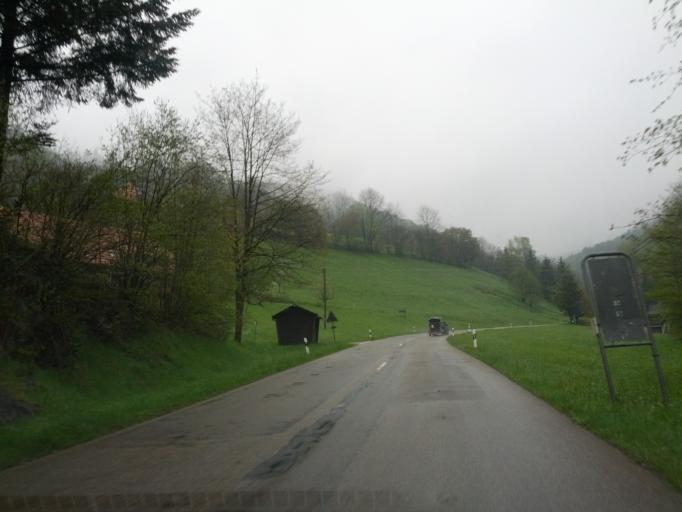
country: DE
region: Baden-Wuerttemberg
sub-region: Freiburg Region
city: Wieden
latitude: 47.8807
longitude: 7.8428
